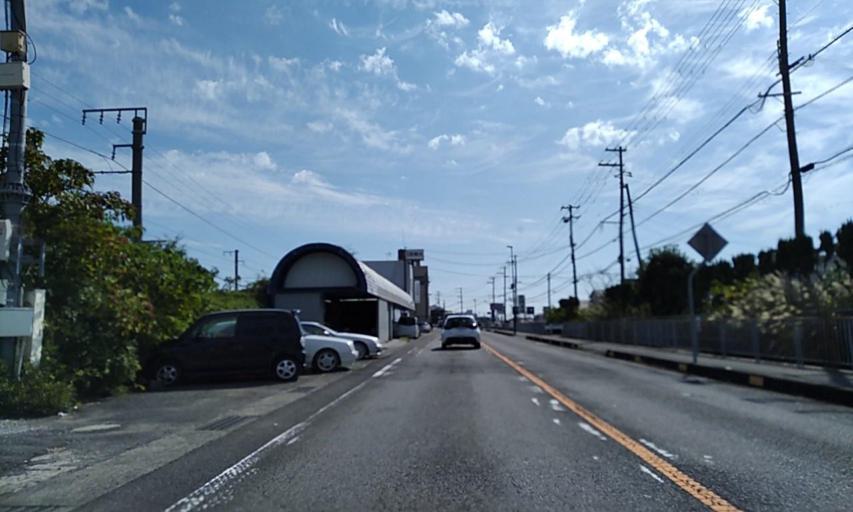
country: JP
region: Wakayama
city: Gobo
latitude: 33.9118
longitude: 135.1494
